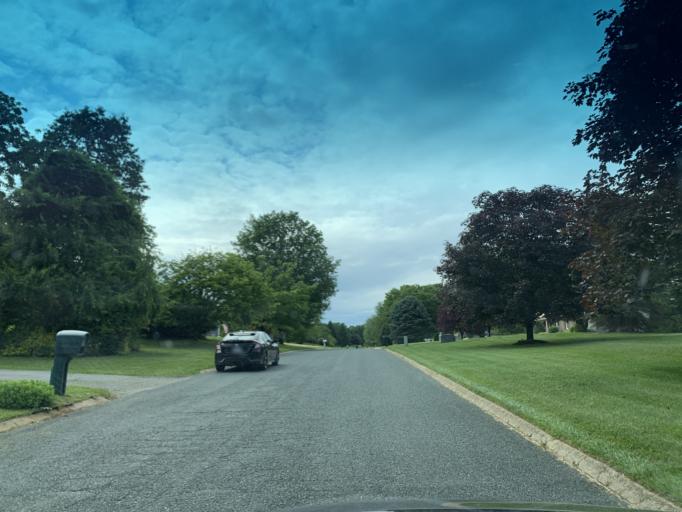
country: US
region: Maryland
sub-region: Harford County
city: Jarrettsville
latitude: 39.5976
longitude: -76.4620
